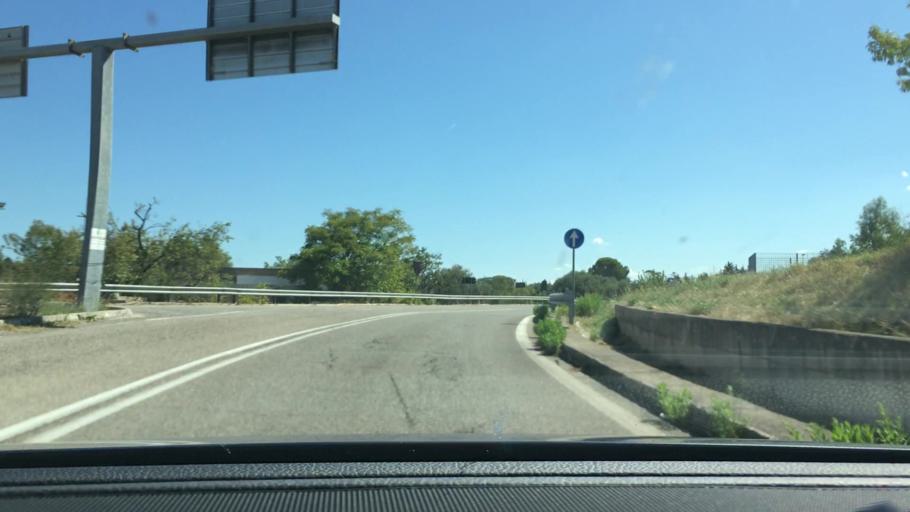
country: IT
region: Apulia
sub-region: Provincia di Bari
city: Bitritto
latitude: 41.0711
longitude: 16.8297
